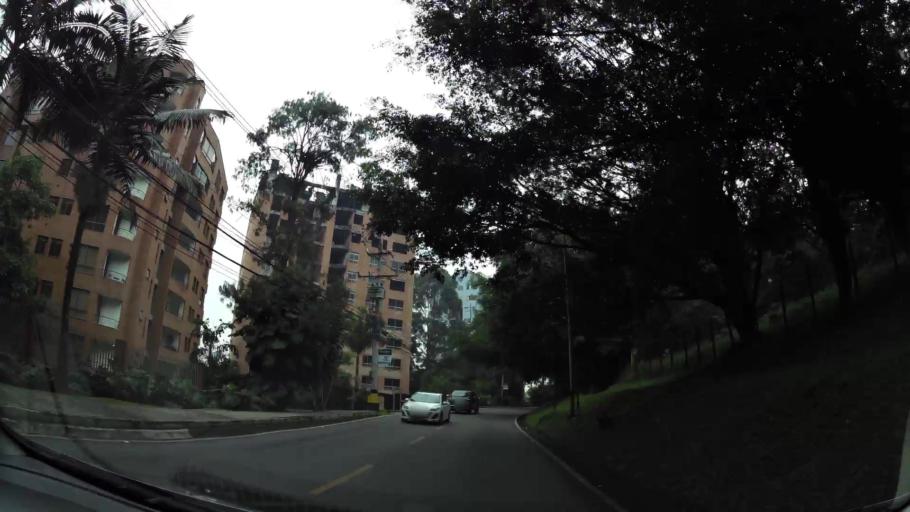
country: CO
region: Antioquia
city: Envigado
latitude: 6.1787
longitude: -75.5675
